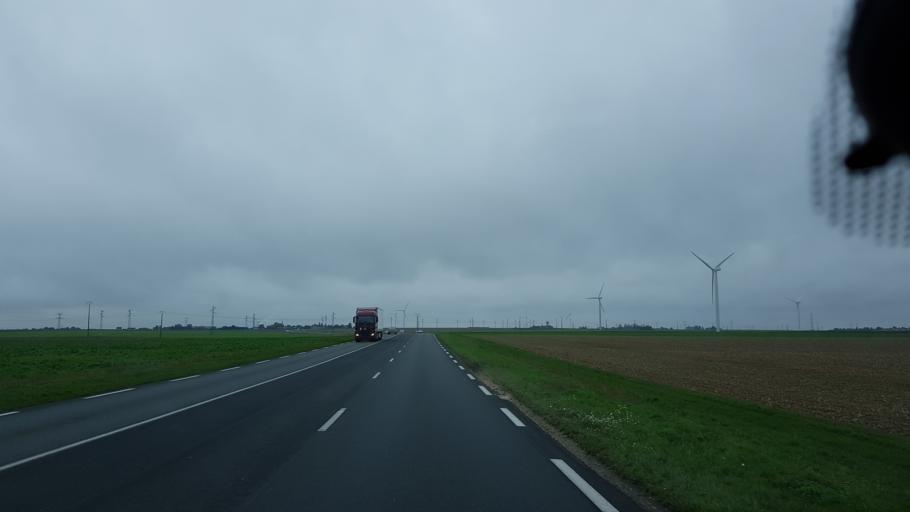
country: FR
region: Centre
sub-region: Departement d'Eure-et-Loir
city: Toury
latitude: 48.1607
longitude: 1.9120
